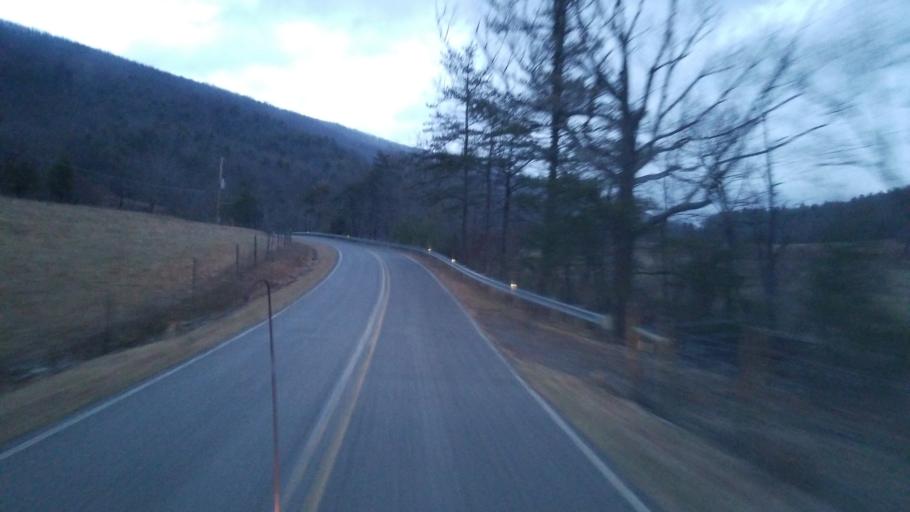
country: US
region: Virginia
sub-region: Pulaski County
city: Pulaski
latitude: 37.1339
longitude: -80.8526
